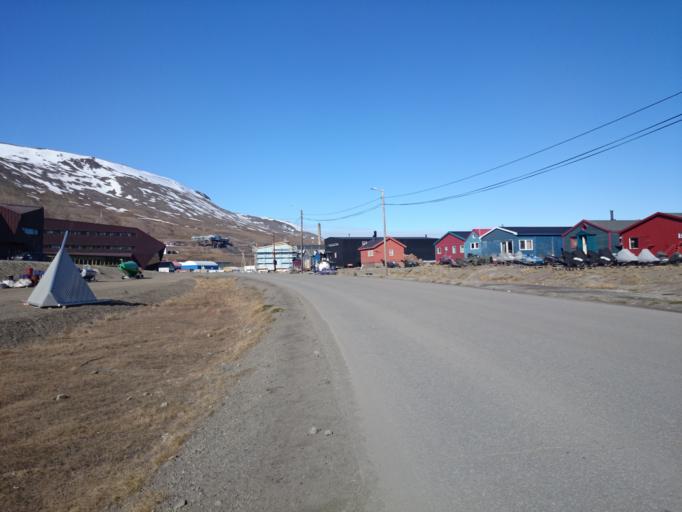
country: SJ
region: Svalbard
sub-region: Spitsbergen
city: Longyearbyen
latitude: 78.2230
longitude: 15.6581
